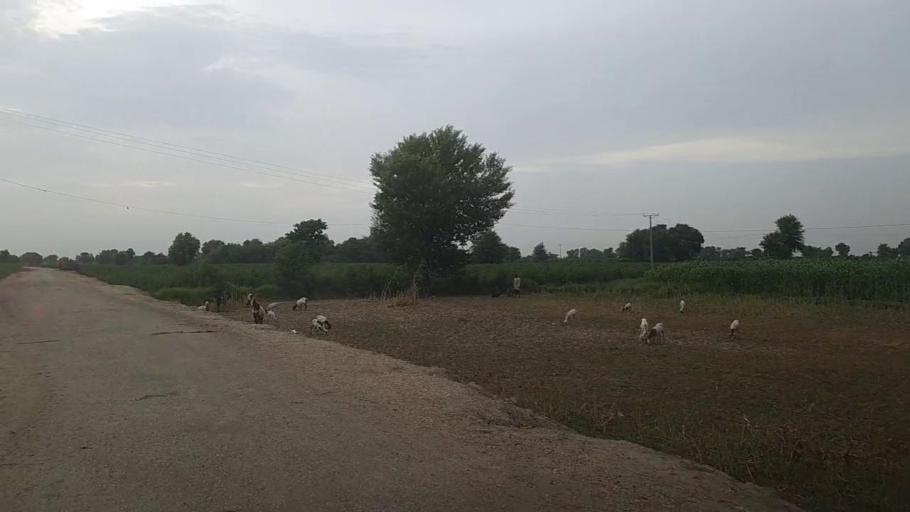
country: PK
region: Sindh
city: Karaundi
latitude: 26.9578
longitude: 68.3570
